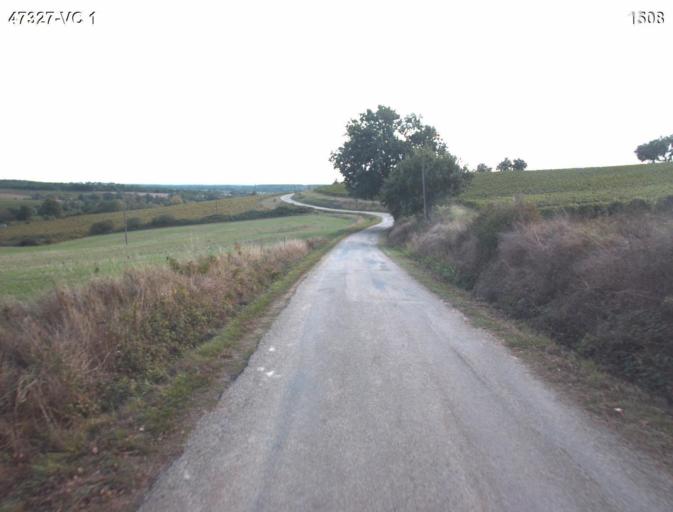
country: FR
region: Aquitaine
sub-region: Departement du Lot-et-Garonne
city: Barbaste
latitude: 44.1980
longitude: 0.2577
